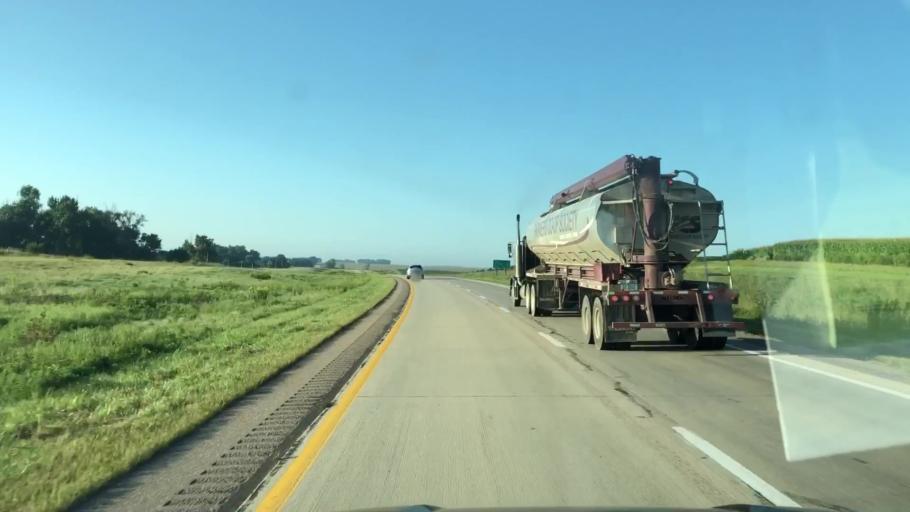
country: US
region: Iowa
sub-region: Sioux County
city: Alton
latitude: 43.0484
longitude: -95.9199
